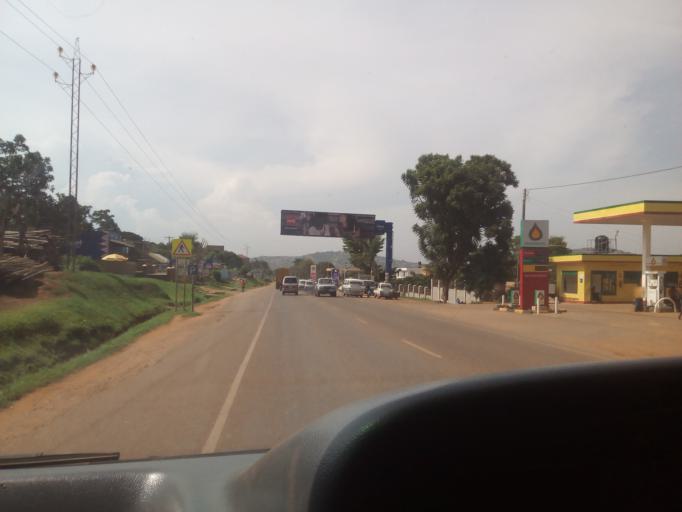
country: UG
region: Central Region
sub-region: Wakiso District
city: Kajansi
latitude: 0.1981
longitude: 32.5398
